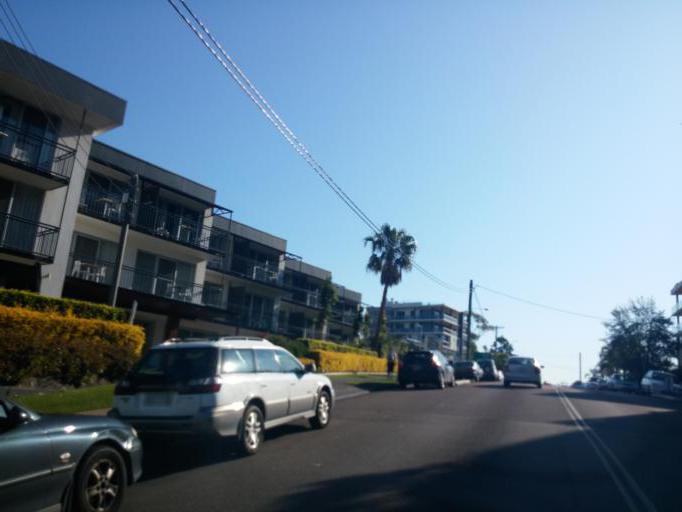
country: AU
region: New South Wales
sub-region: Port Stephens Shire
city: Nelson Bay
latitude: -32.7204
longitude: 152.1431
